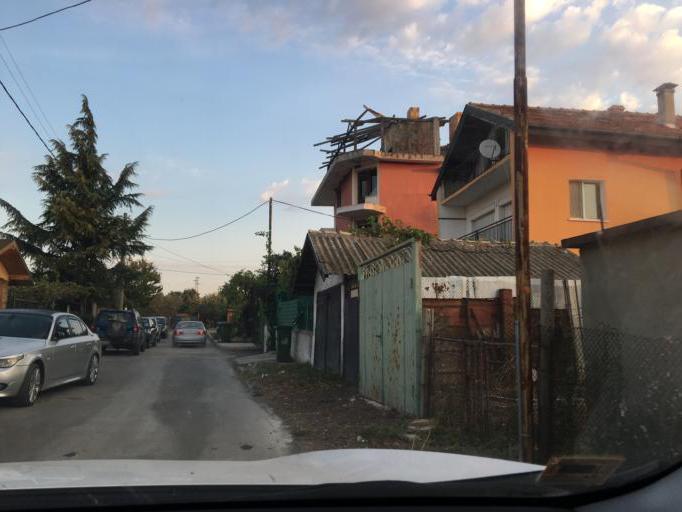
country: BG
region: Burgas
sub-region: Obshtina Burgas
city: Burgas
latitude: 42.6133
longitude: 27.4951
